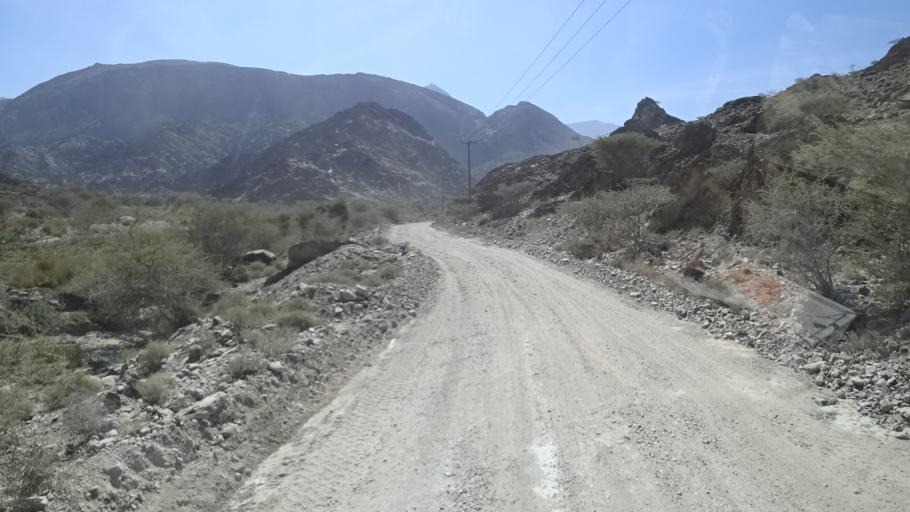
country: OM
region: Al Batinah
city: Bayt al `Awabi
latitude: 23.2332
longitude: 57.4260
